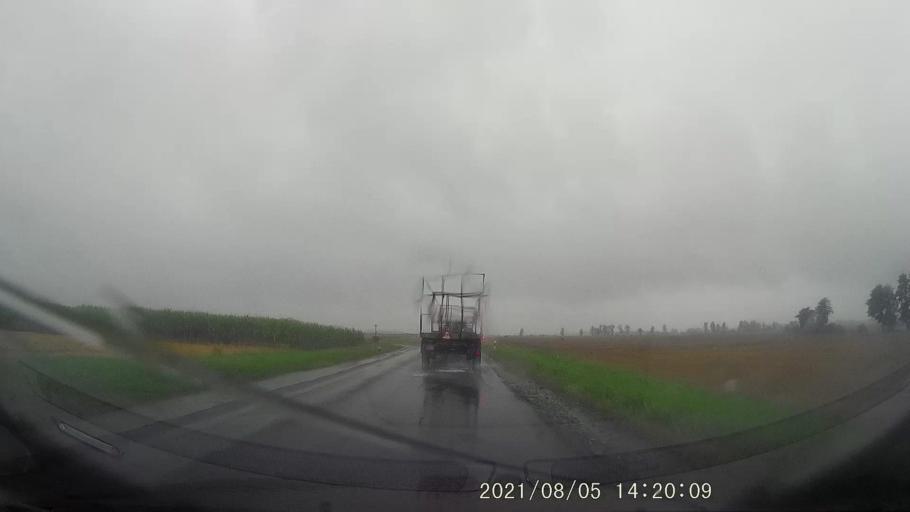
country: PL
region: Opole Voivodeship
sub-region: Powiat prudnicki
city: Biala
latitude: 50.4688
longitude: 17.6825
